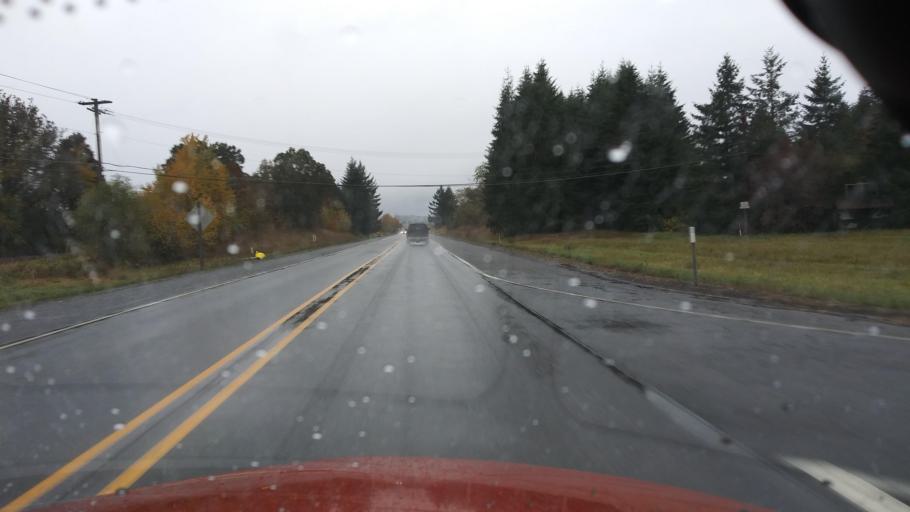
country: US
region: Oregon
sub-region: Washington County
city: Forest Grove
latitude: 45.4851
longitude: -123.1269
